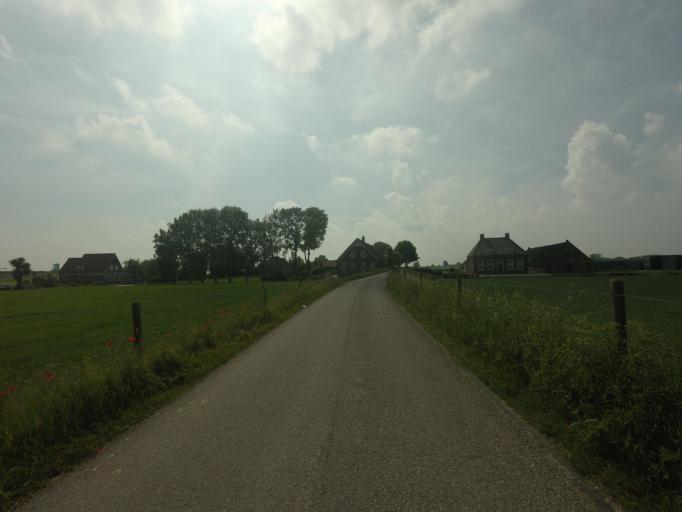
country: NL
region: Utrecht
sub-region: Gemeente IJsselstein
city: IJsselstein
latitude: 51.9996
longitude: 5.0608
